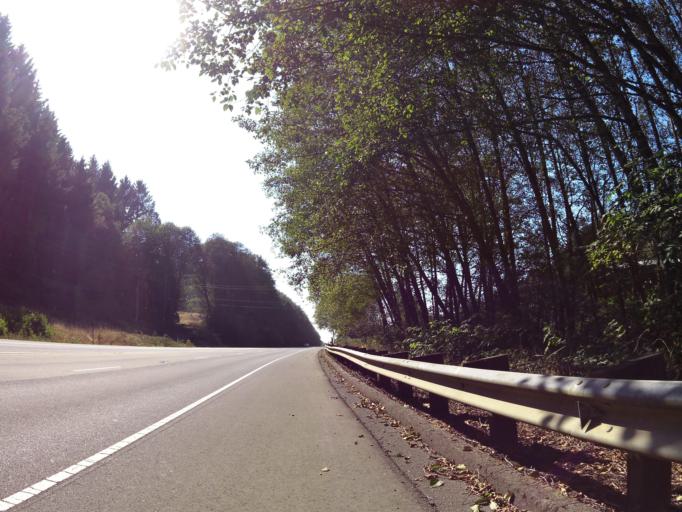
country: US
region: Oregon
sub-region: Tillamook County
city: Pacific City
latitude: 45.1485
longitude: -123.9599
